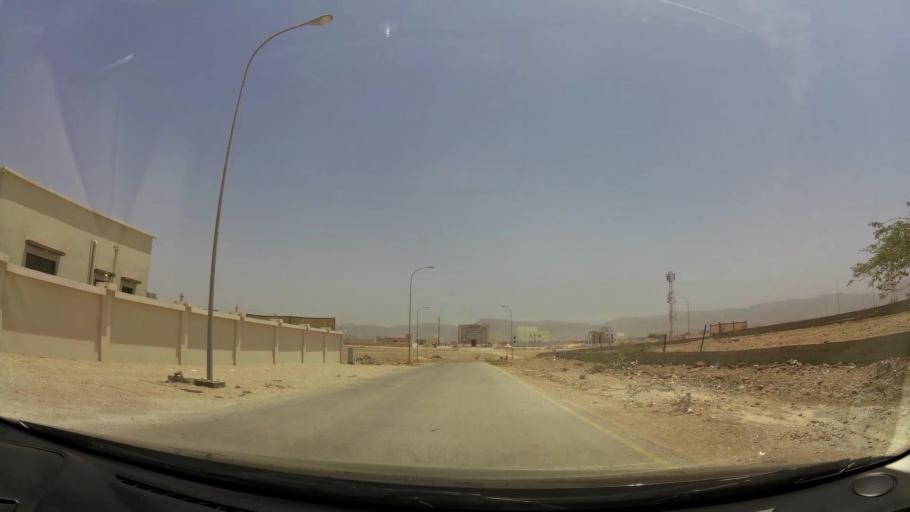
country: OM
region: Zufar
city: Salalah
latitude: 17.0898
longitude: 54.1850
